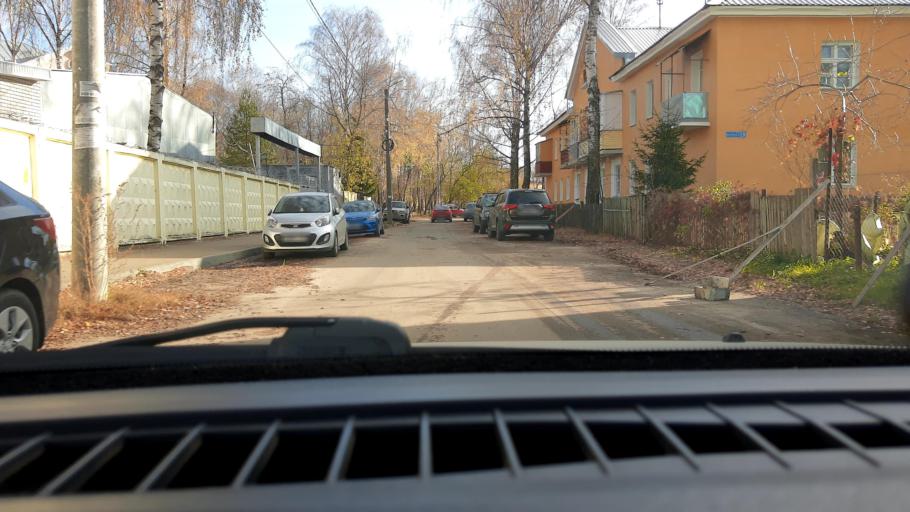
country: RU
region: Nizjnij Novgorod
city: Neklyudovo
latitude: 56.3537
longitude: 43.8503
